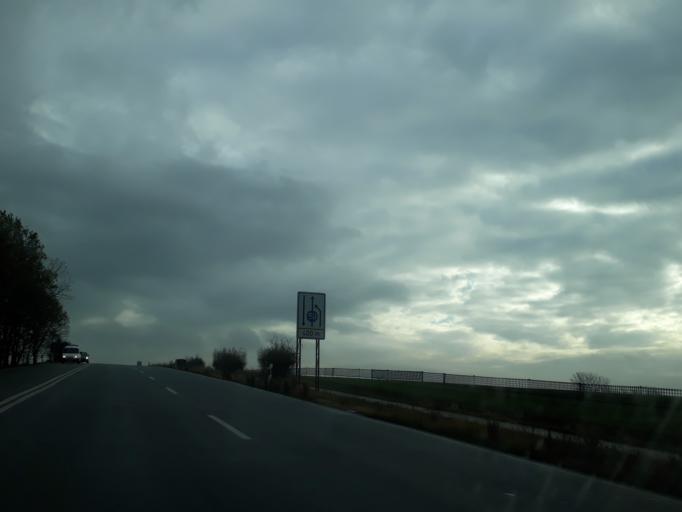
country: DE
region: Saxony
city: Hochkirch
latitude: 51.1284
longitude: 14.6191
